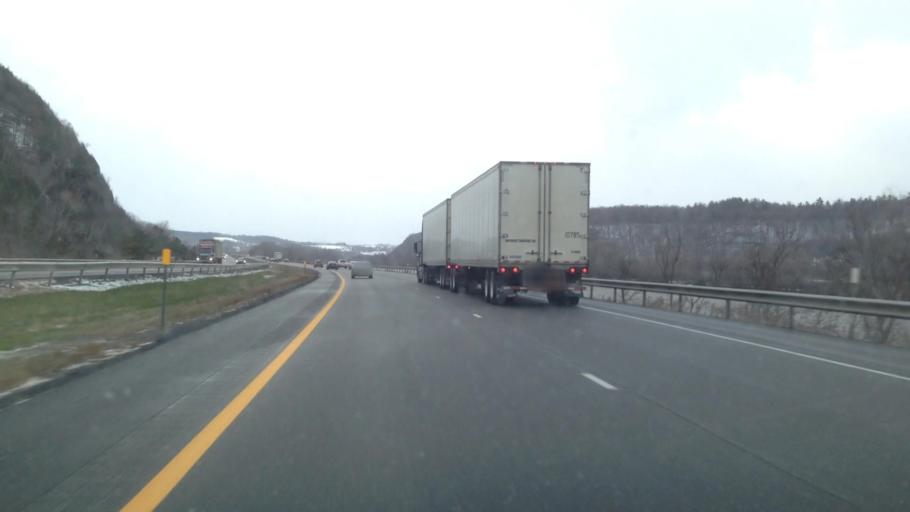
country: US
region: New York
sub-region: Montgomery County
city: Canajoharie
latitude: 42.8961
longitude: -74.4819
